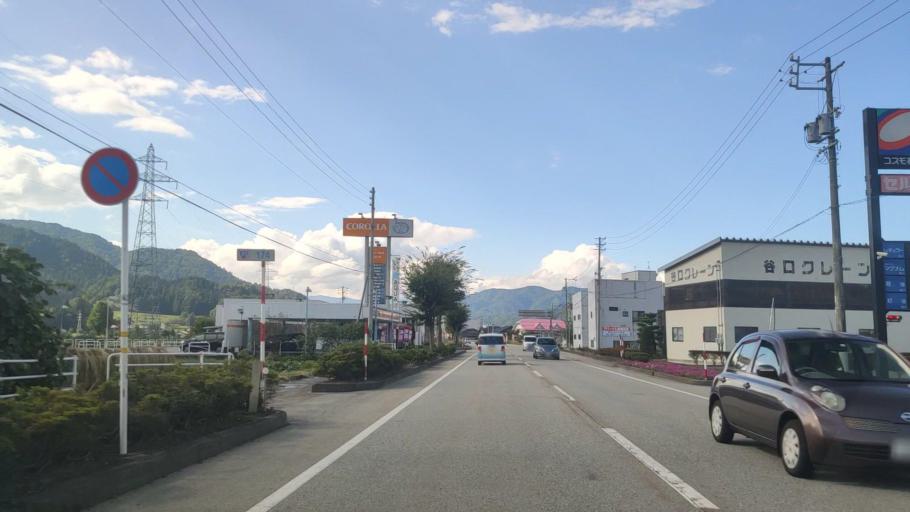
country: JP
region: Gifu
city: Takayama
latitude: 36.2242
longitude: 137.1895
